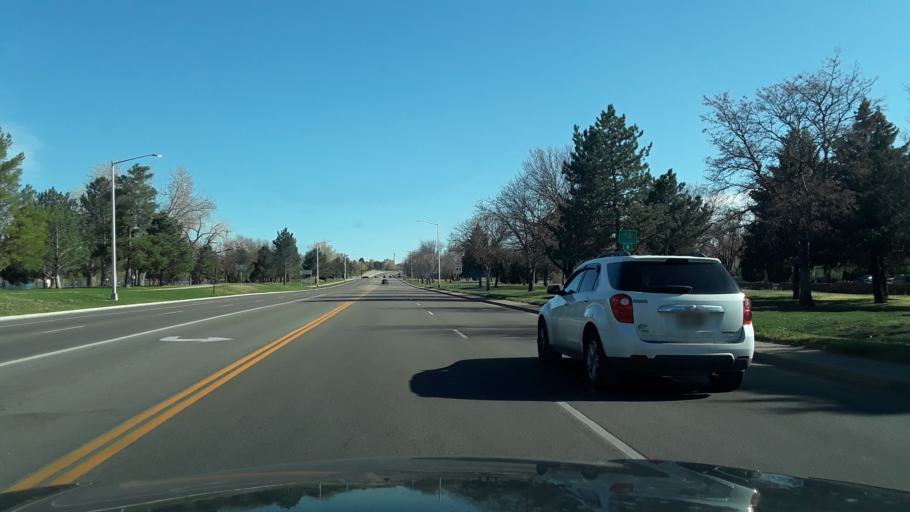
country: US
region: Colorado
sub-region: Pueblo County
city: Pueblo
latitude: 38.2638
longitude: -104.6618
